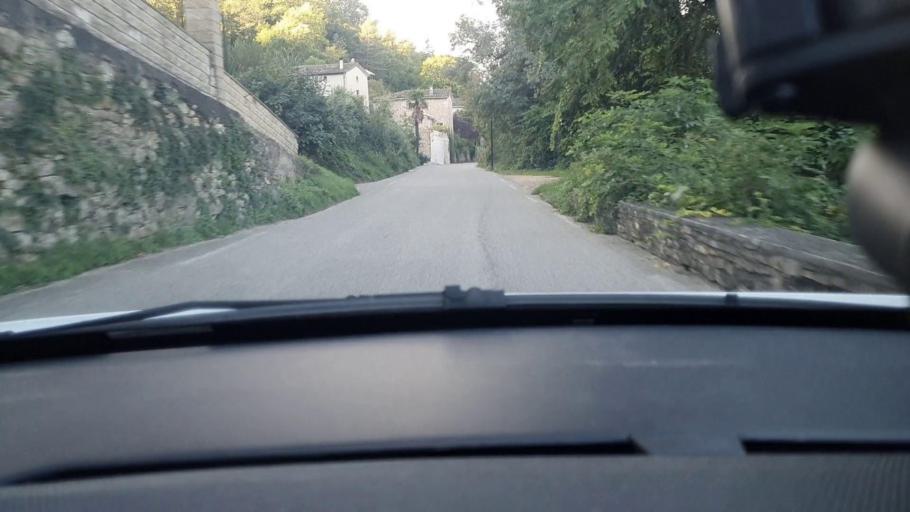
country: FR
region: Languedoc-Roussillon
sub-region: Departement du Gard
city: Barjac
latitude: 44.2373
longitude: 4.2934
